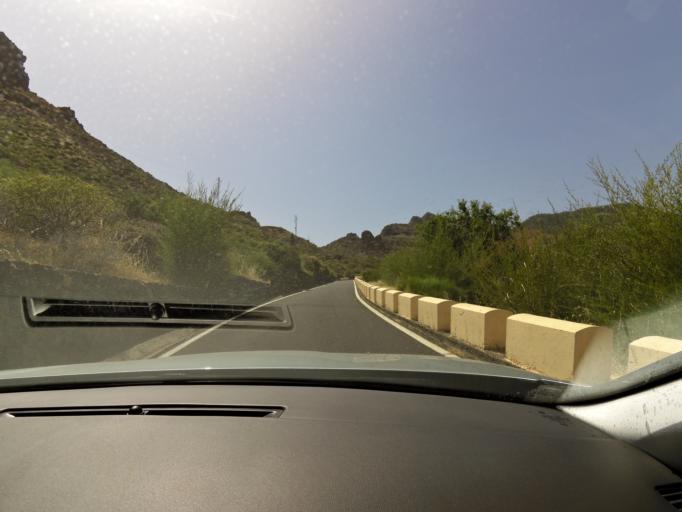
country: ES
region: Canary Islands
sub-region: Provincia de Santa Cruz de Tenerife
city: Santiago del Teide
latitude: 28.2971
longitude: -16.8187
